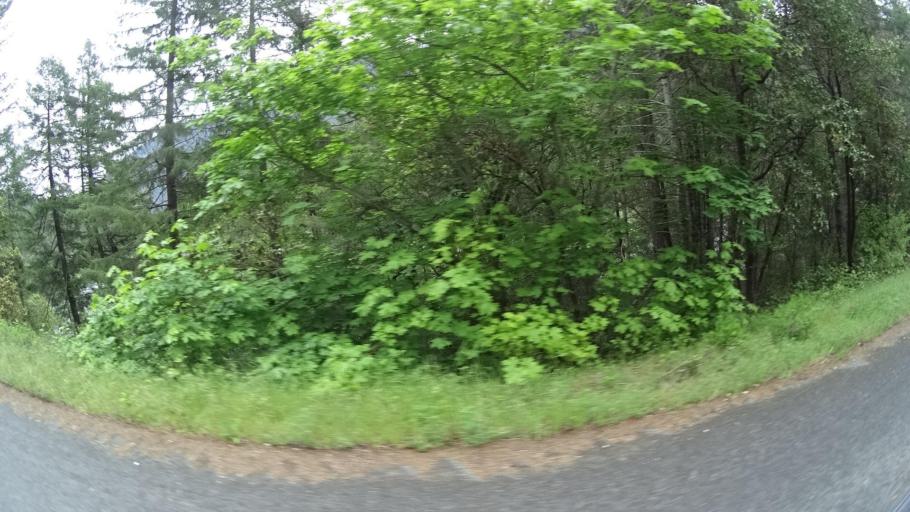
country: US
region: California
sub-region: Humboldt County
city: Willow Creek
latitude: 41.3263
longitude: -123.5257
